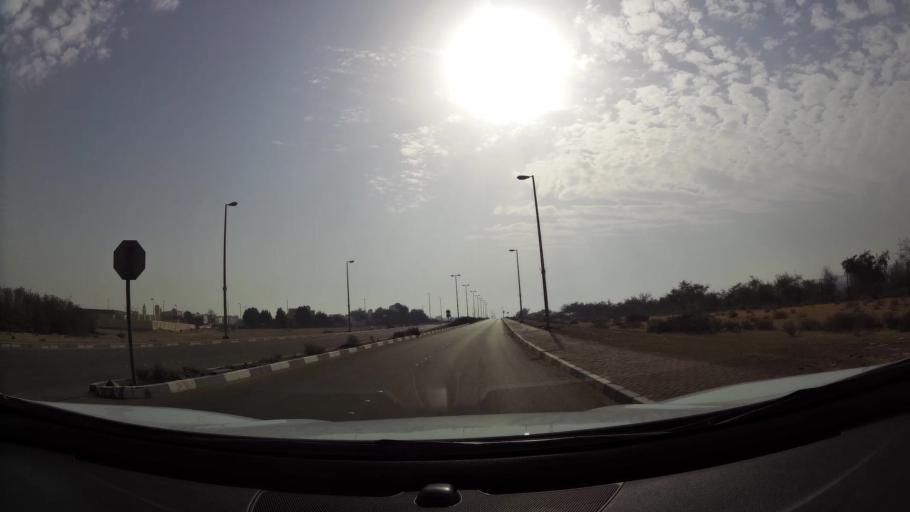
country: AE
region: Abu Dhabi
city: Abu Dhabi
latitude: 24.2553
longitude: 54.7131
